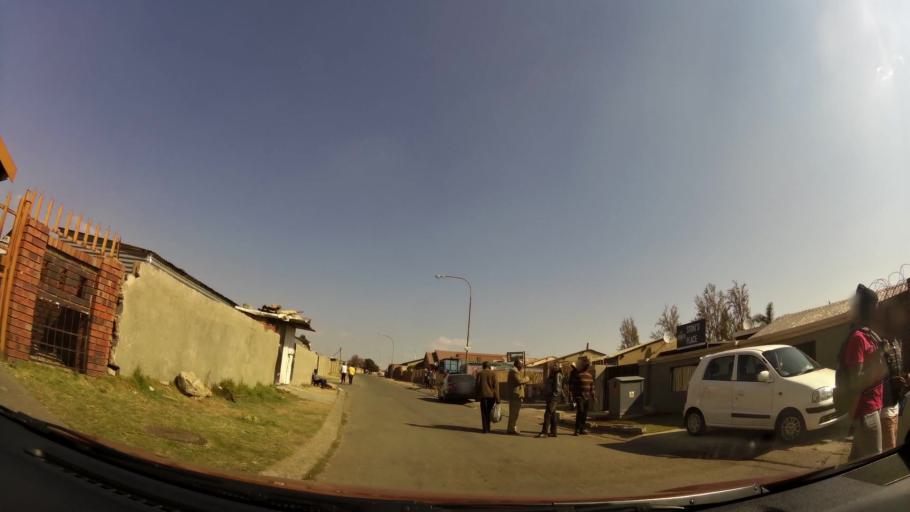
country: ZA
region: Gauteng
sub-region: City of Johannesburg Metropolitan Municipality
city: Johannesburg
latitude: -26.2382
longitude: 27.9552
